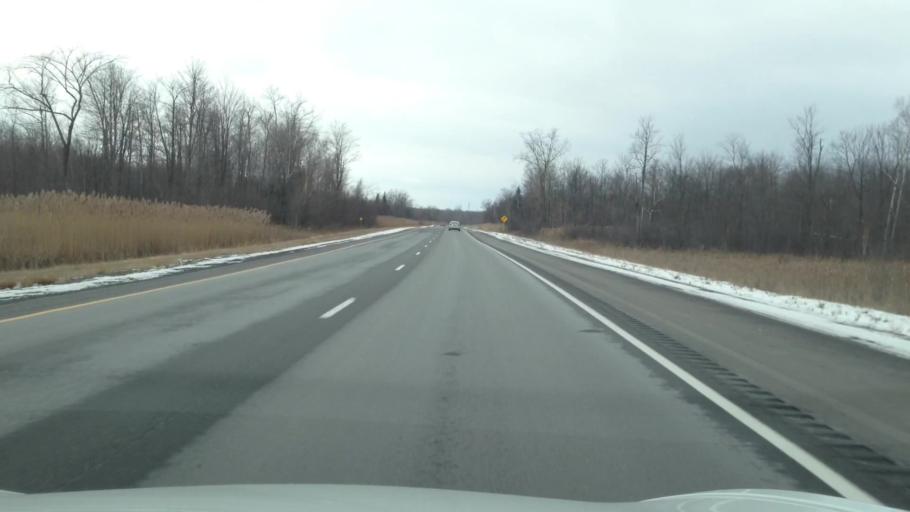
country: CA
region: Ontario
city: Bourget
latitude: 45.3306
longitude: -75.2927
